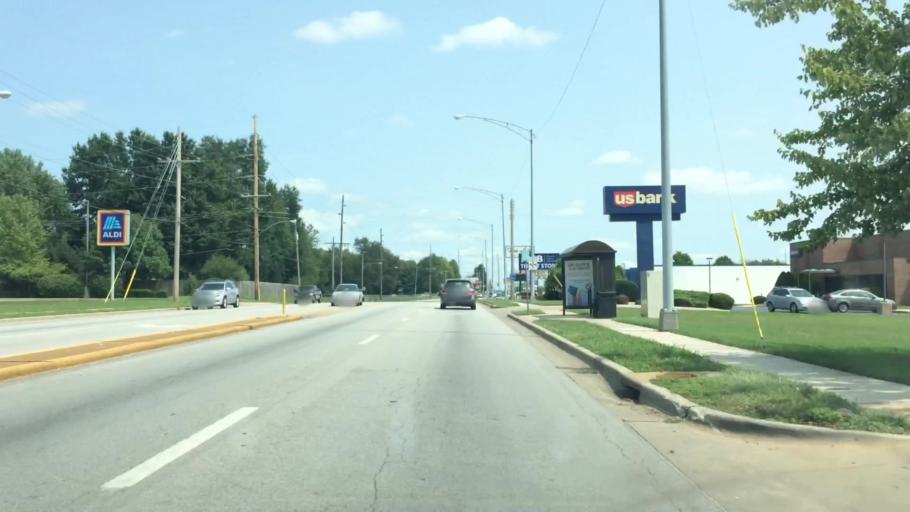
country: US
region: Missouri
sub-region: Greene County
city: Springfield
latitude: 37.1599
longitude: -93.2907
